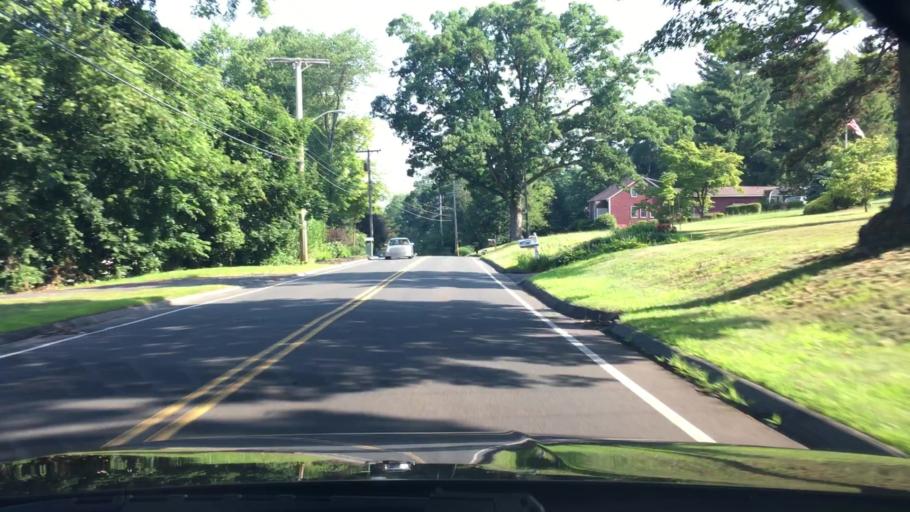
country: US
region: Massachusetts
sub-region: Hampden County
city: East Longmeadow
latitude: 42.0571
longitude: -72.5117
